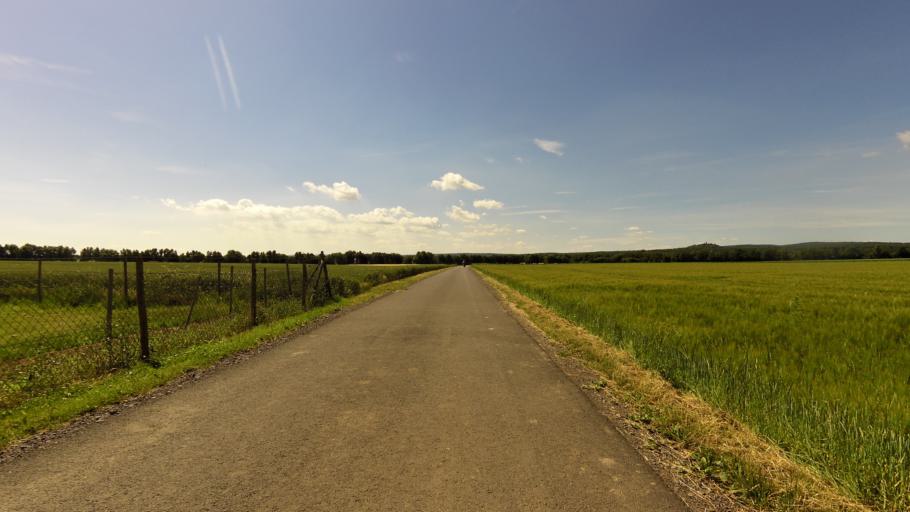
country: DE
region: North Rhine-Westphalia
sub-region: Regierungsbezirk Koln
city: Rheinbach
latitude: 50.6210
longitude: 6.9891
